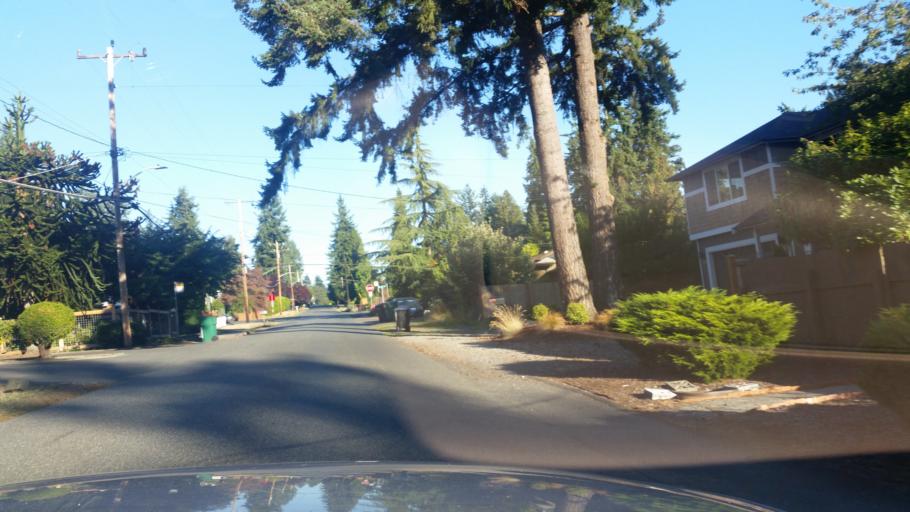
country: US
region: Washington
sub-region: King County
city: Shoreline
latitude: 47.7251
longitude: -122.3621
